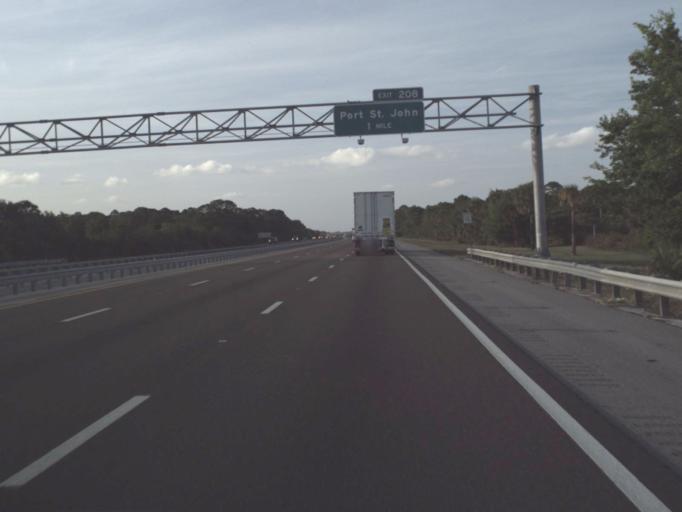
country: US
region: Florida
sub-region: Brevard County
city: Port Saint John
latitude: 28.4316
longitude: -80.8202
